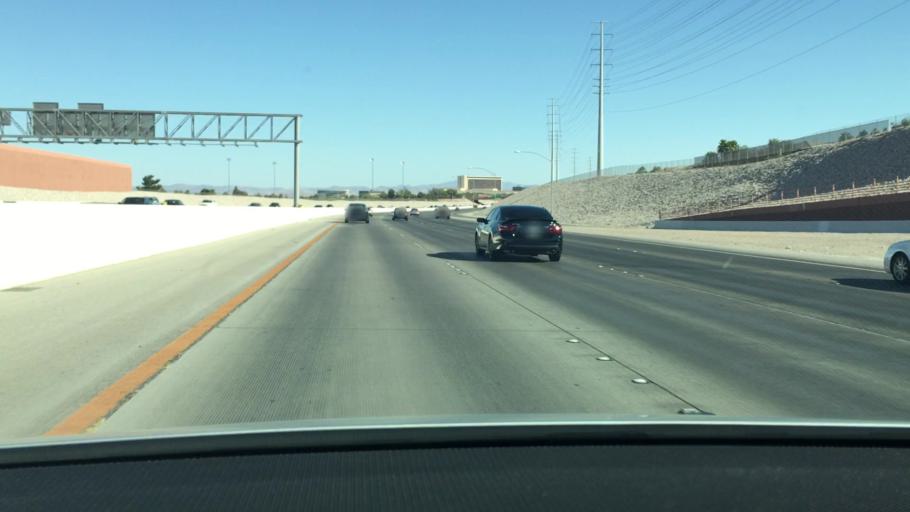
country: US
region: Nevada
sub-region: Clark County
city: Summerlin South
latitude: 36.1773
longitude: -115.3394
